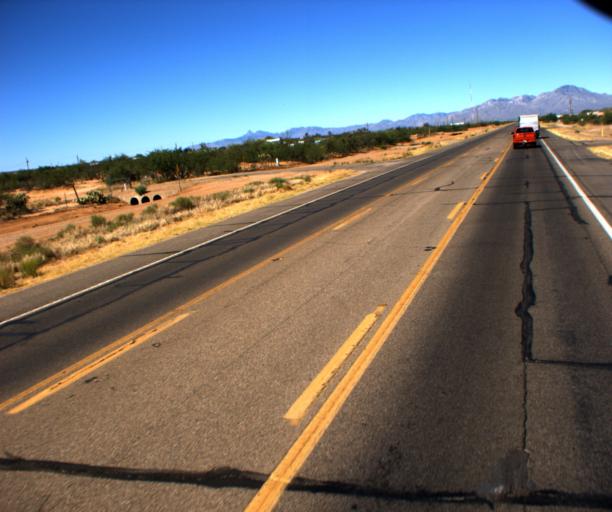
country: US
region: Arizona
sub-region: Pima County
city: Three Points
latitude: 32.0869
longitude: -111.2879
